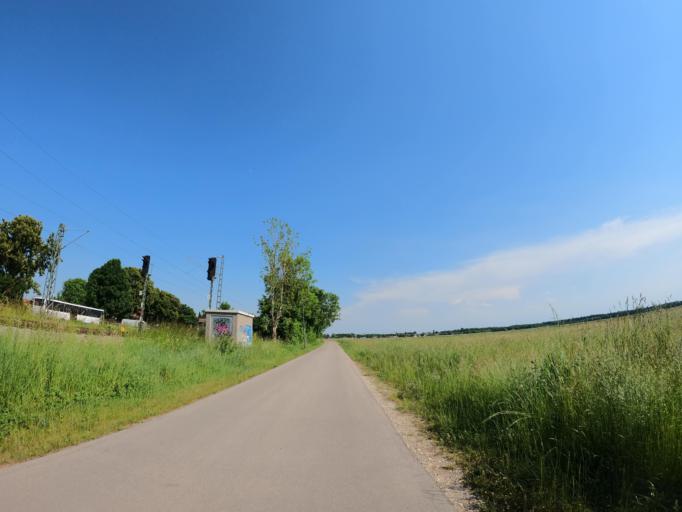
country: DE
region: Bavaria
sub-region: Upper Bavaria
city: Hohenbrunn
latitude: 48.0456
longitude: 11.6997
